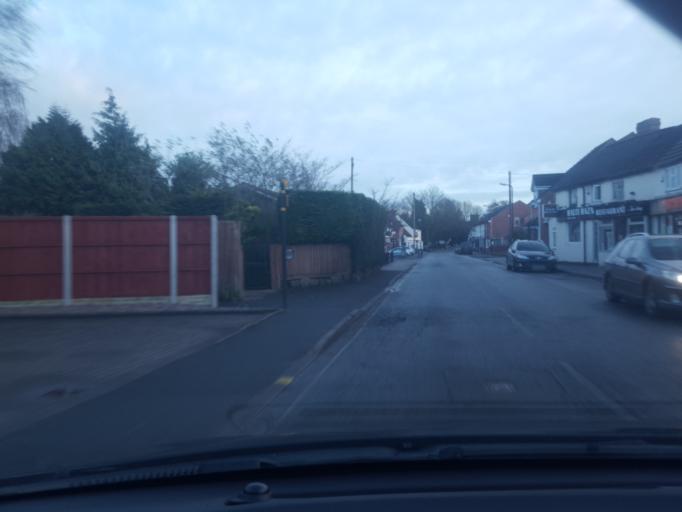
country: GB
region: England
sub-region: Shropshire
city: Albrighton
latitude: 52.6362
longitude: -2.2817
